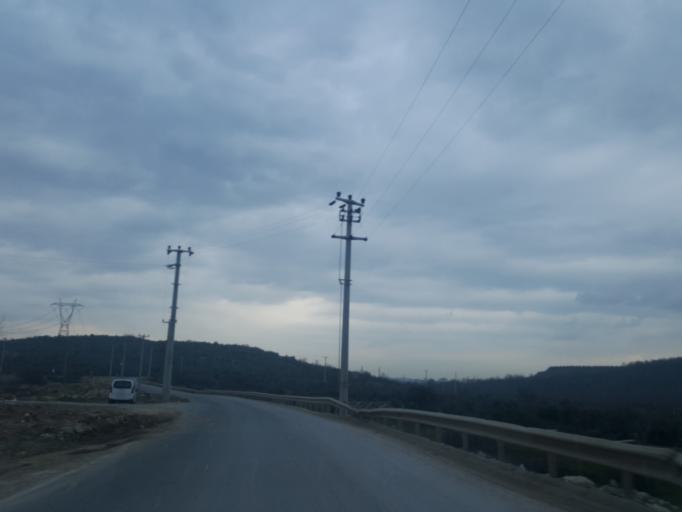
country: TR
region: Kocaeli
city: Tavsanli
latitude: 40.8578
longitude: 29.5738
